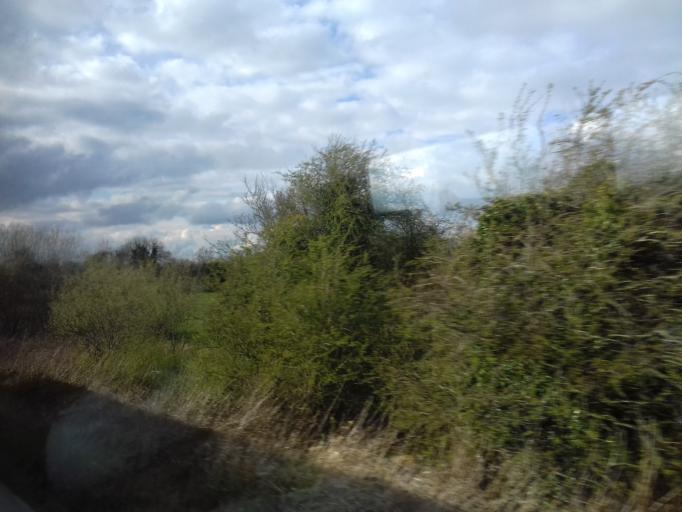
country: IE
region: Leinster
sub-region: An Iarmhi
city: Kinnegad
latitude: 53.4799
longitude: -7.0700
